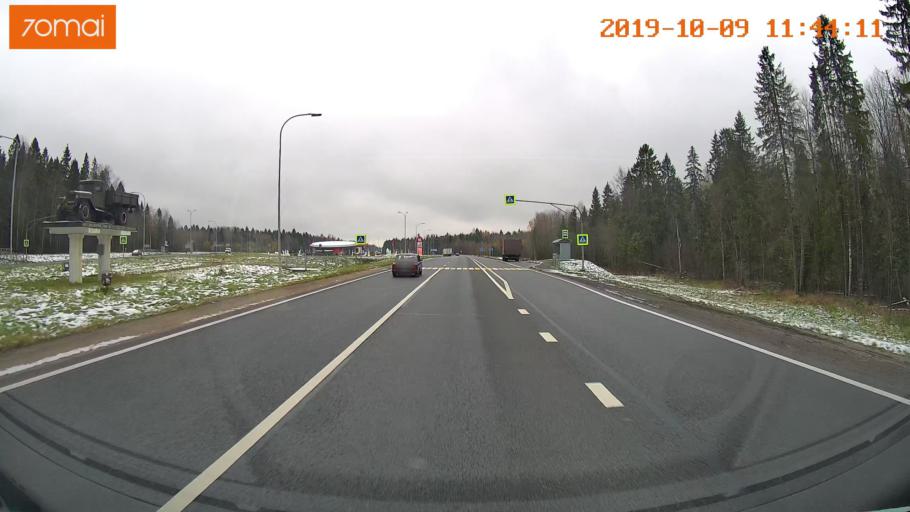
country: RU
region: Vologda
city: Gryazovets
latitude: 58.8867
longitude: 40.1899
